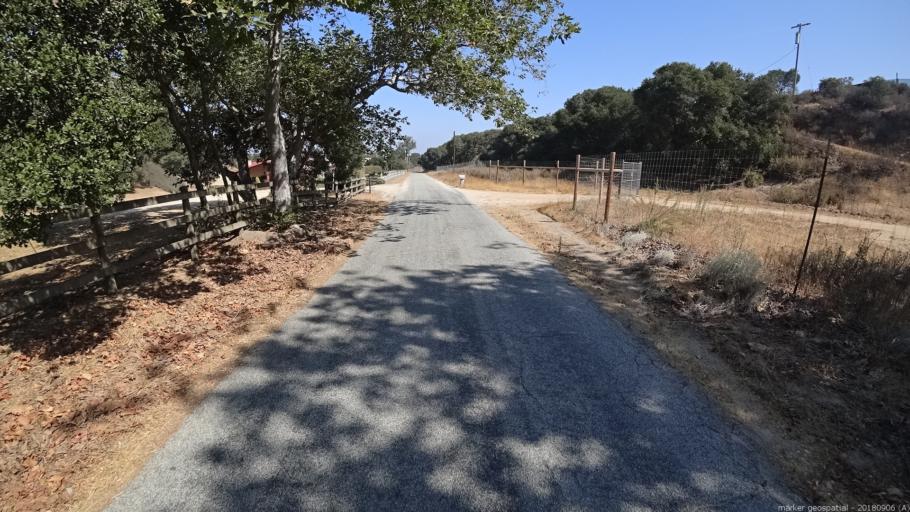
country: US
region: California
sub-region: Monterey County
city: Chualar
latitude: 36.5798
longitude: -121.6071
